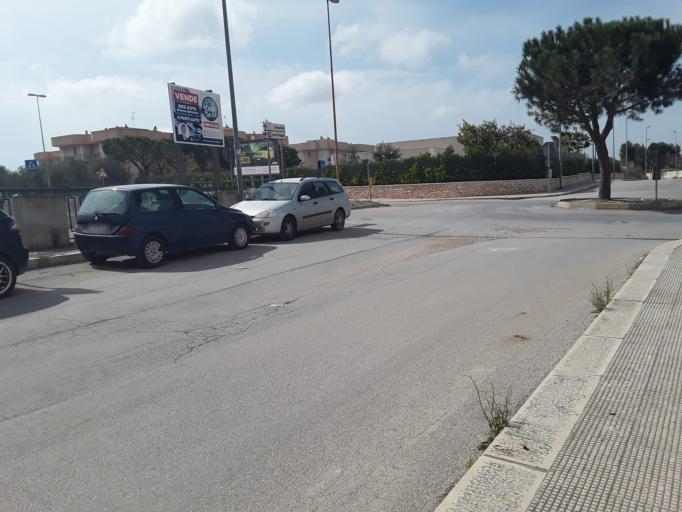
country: IT
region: Apulia
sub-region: Provincia di Bari
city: Ruvo di Puglia
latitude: 41.1227
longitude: 16.4773
